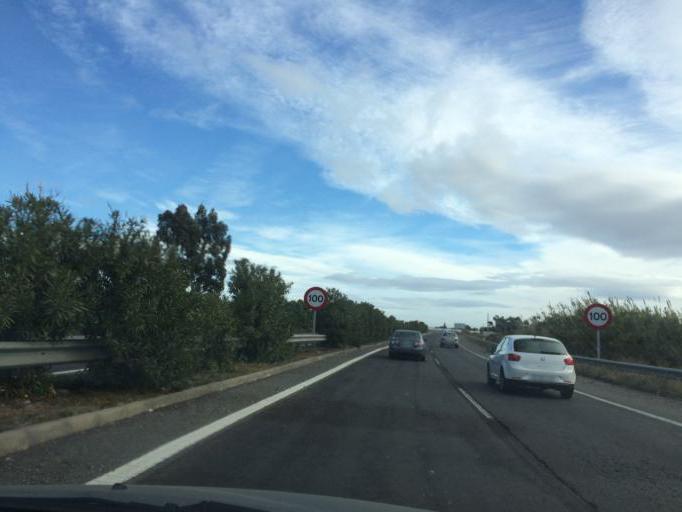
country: ES
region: Andalusia
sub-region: Provincia de Almeria
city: Viator
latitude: 36.8447
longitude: -2.3955
